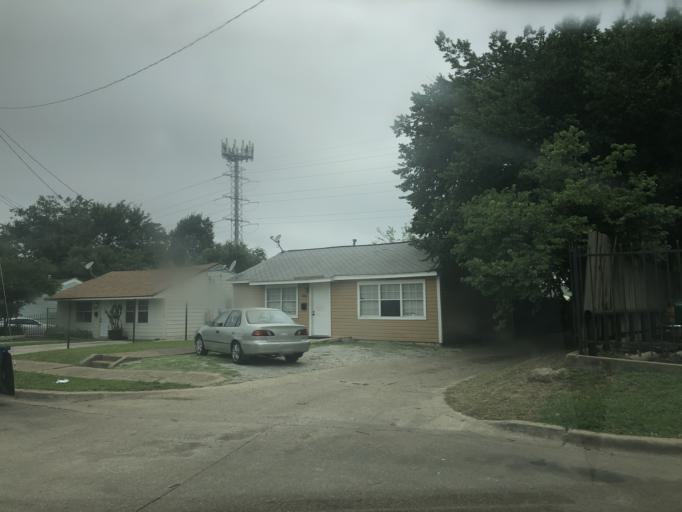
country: US
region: Texas
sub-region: Dallas County
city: Farmers Branch
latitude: 32.8652
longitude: -96.8679
